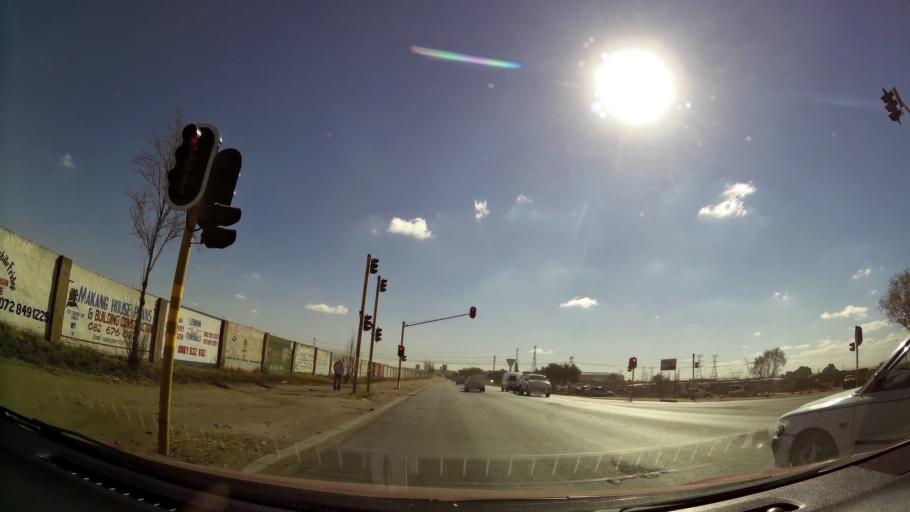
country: ZA
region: Gauteng
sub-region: City of Johannesburg Metropolitan Municipality
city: Modderfontein
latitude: -26.0390
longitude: 28.1749
